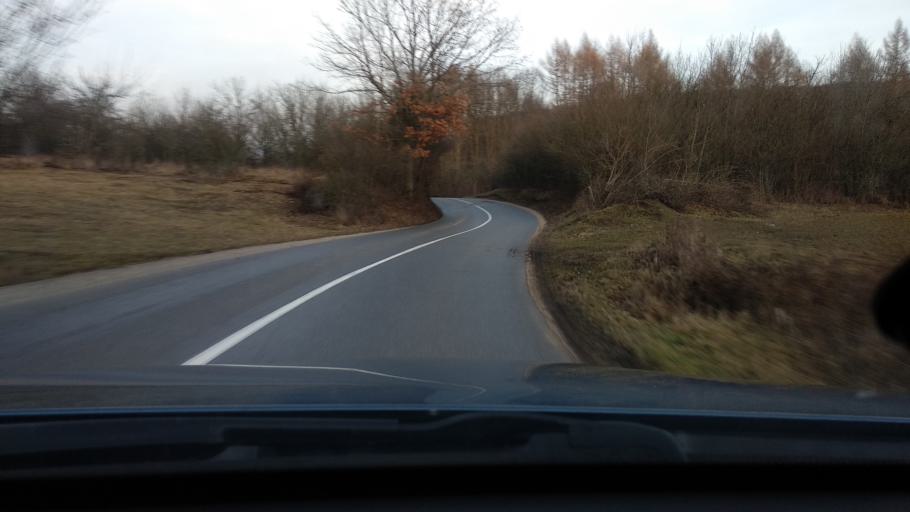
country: SK
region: Nitriansky
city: Trencianske Teplice
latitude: 48.8379
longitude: 18.1976
